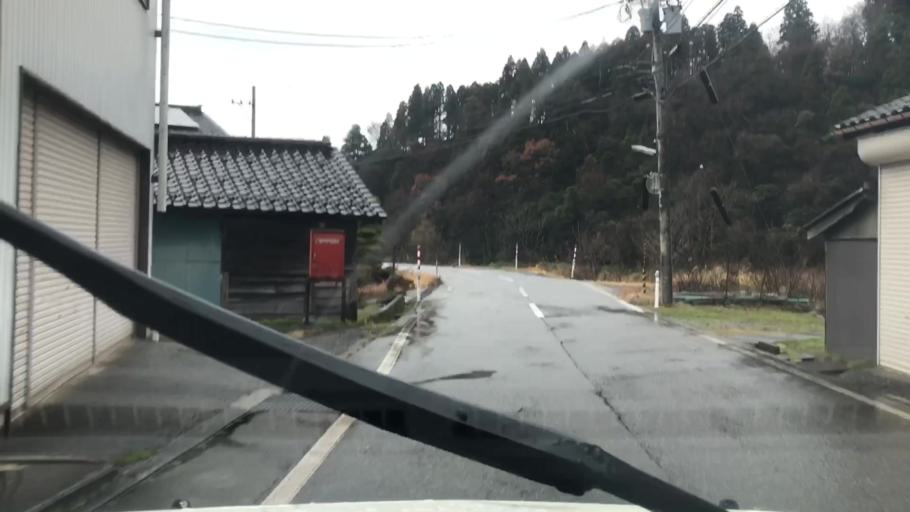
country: JP
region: Toyama
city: Kamiichi
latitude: 36.6048
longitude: 137.2926
